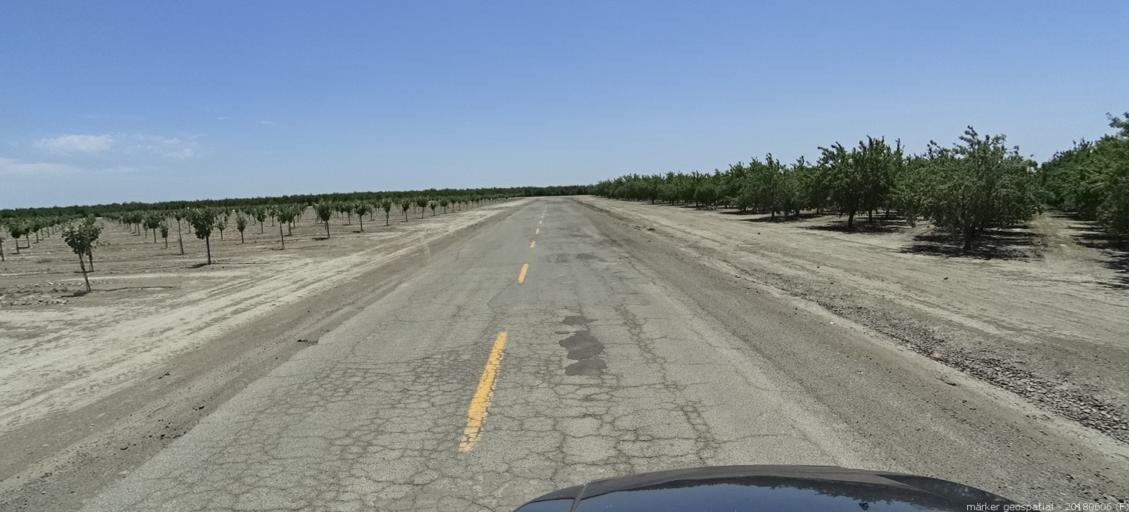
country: US
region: California
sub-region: Fresno County
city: Mendota
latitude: 36.8320
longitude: -120.3783
